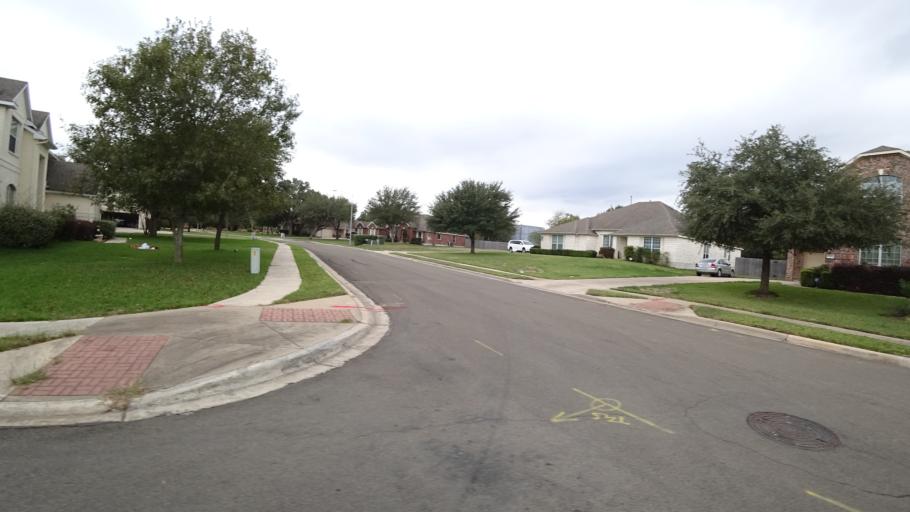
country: US
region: Texas
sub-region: Travis County
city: Shady Hollow
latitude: 30.1536
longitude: -97.8614
